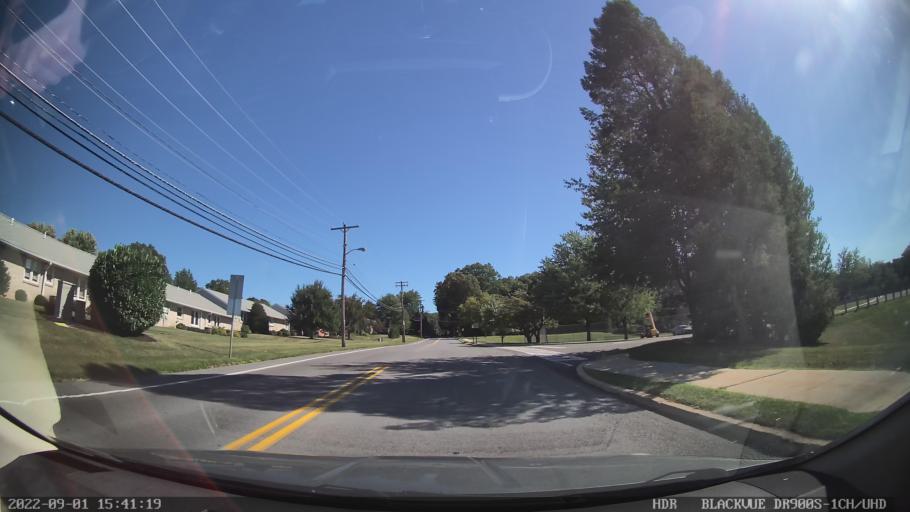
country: US
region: Pennsylvania
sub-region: Berks County
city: Topton
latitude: 40.4981
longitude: -75.7018
